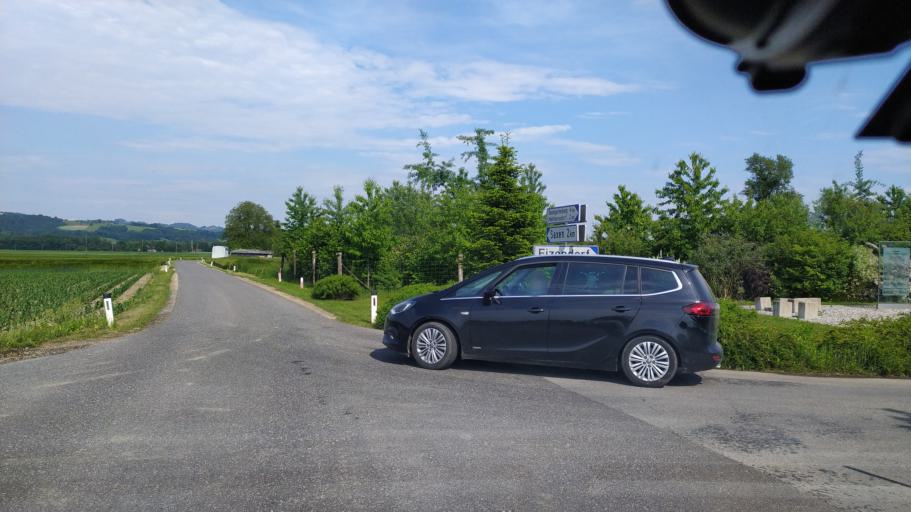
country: AT
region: Upper Austria
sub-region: Politischer Bezirk Perg
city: Bad Kreuzen
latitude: 48.1952
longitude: 14.7689
